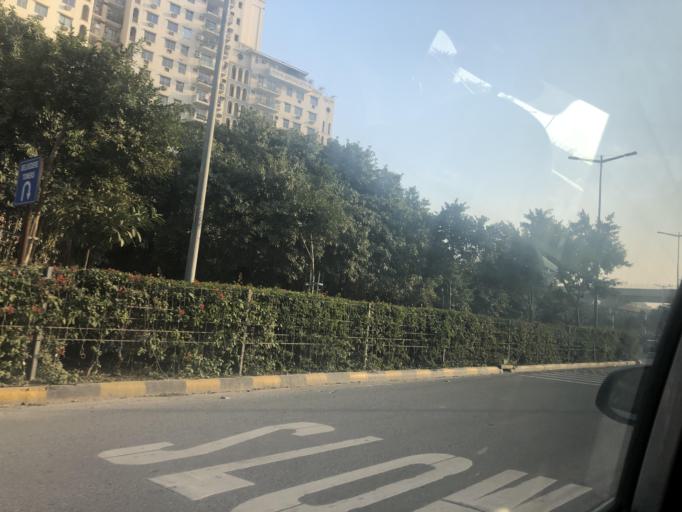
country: IN
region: Haryana
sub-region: Gurgaon
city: Gurgaon
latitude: 28.4909
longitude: 77.0904
